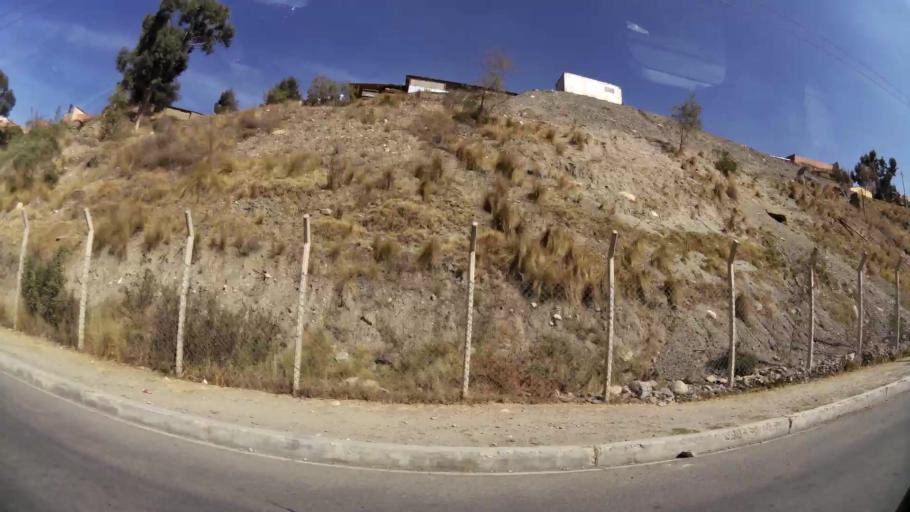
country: BO
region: La Paz
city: La Paz
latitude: -16.5076
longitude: -68.1166
